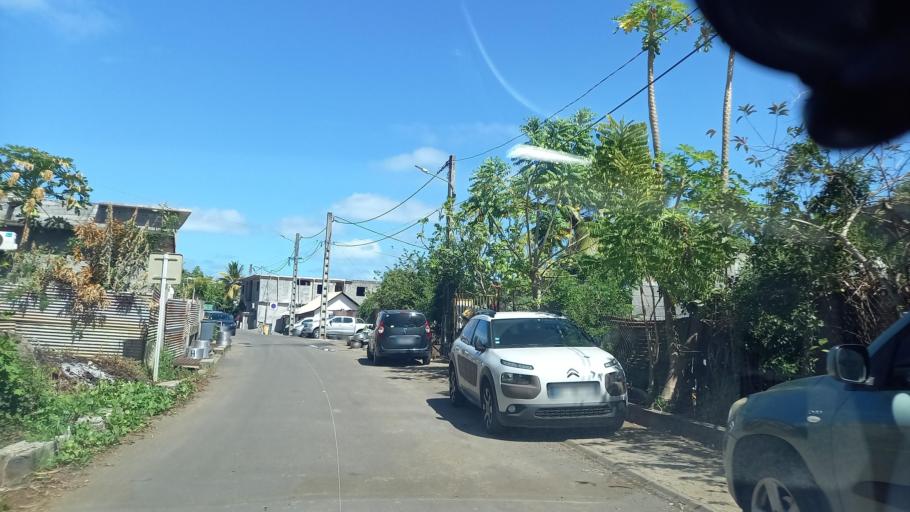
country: YT
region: Kani-Keli
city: Kani Keli
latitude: -12.9627
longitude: 45.1113
